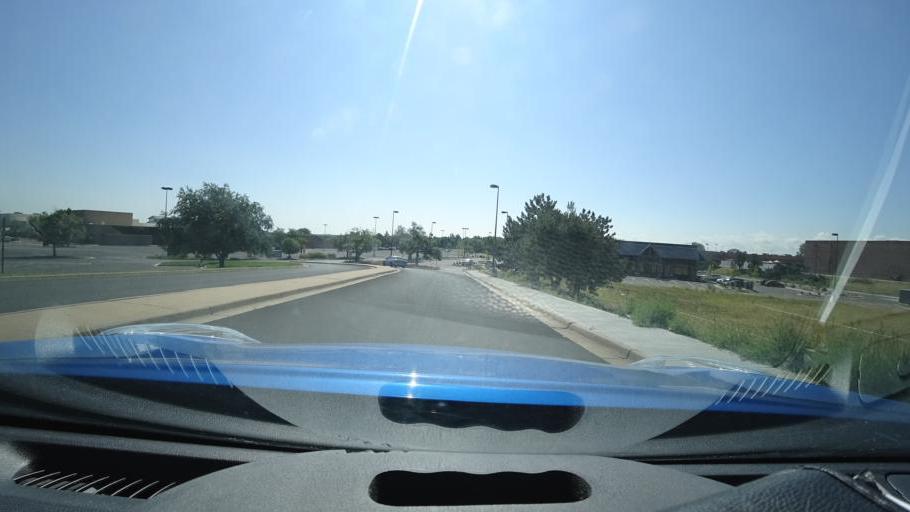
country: US
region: Colorado
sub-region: Adams County
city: Aurora
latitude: 39.7064
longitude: -104.8272
